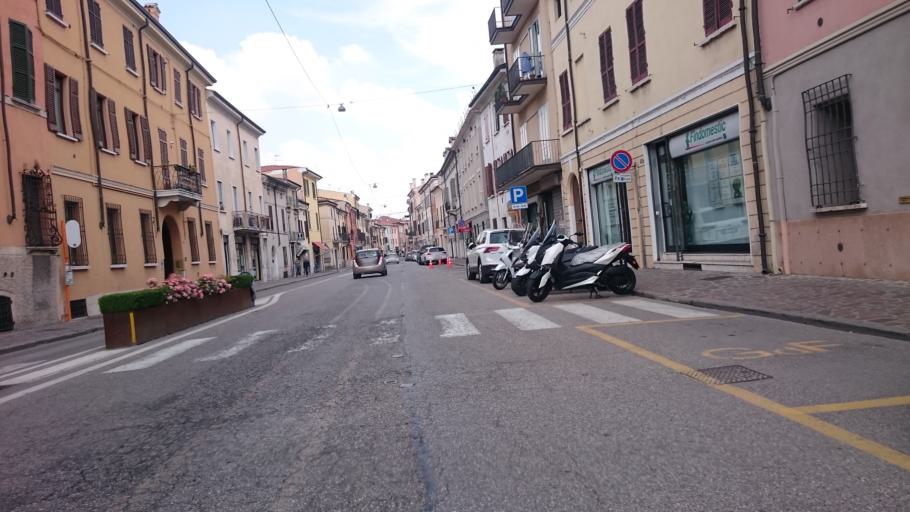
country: IT
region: Lombardy
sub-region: Provincia di Mantova
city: Mantova
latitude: 45.1513
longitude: 10.7961
